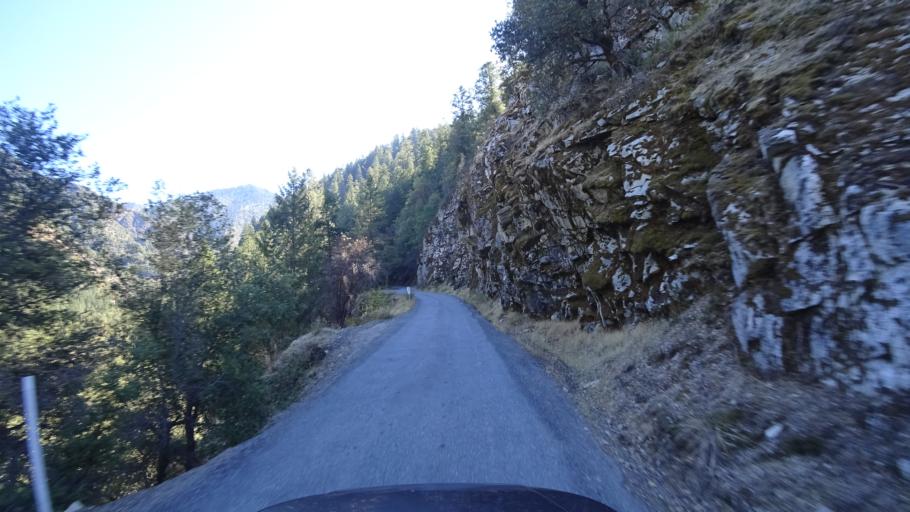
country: US
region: California
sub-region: Siskiyou County
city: Happy Camp
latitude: 41.3406
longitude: -123.3829
